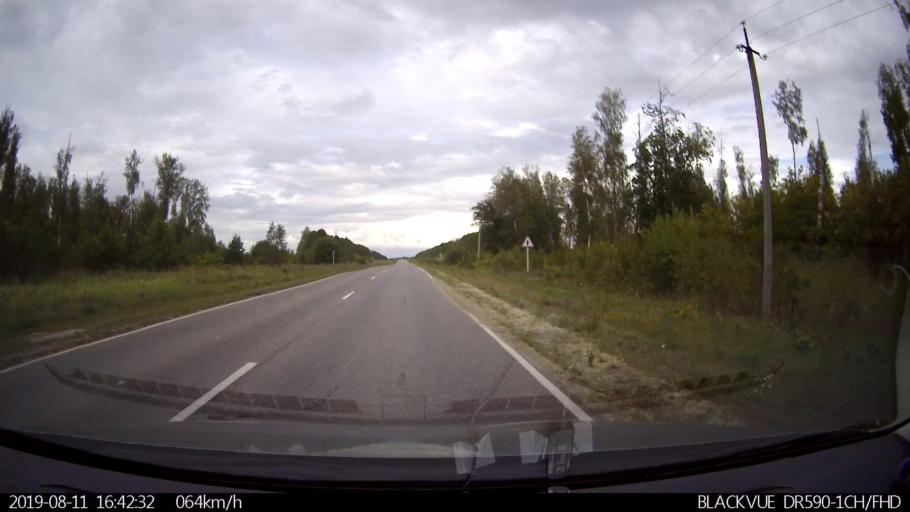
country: RU
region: Ulyanovsk
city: Mayna
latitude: 54.1612
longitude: 47.6631
